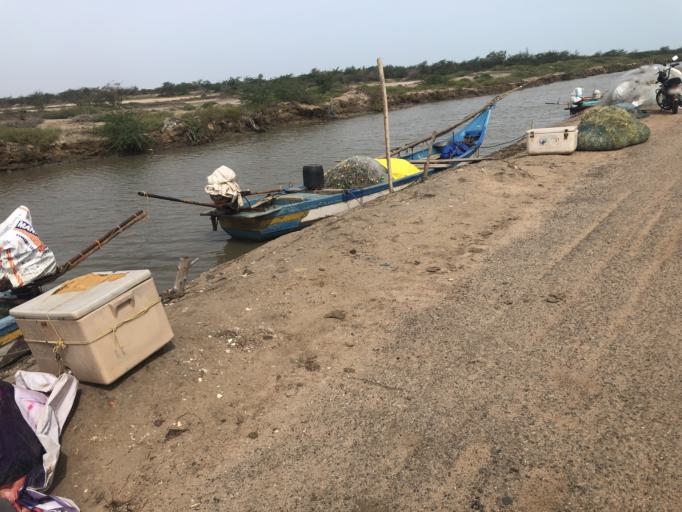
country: IN
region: Tamil Nadu
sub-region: Thanjavur
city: Adirampattinam
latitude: 10.3193
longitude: 79.3806
